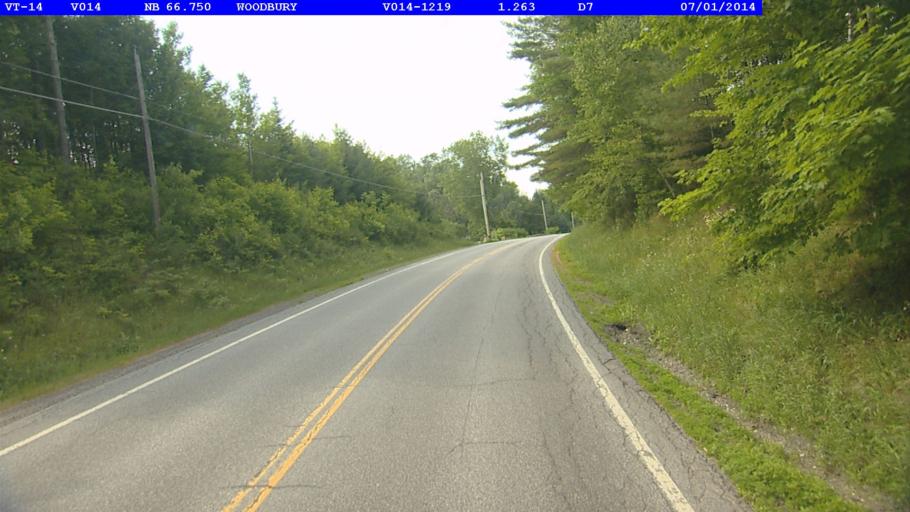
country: US
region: Vermont
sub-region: Caledonia County
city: Hardwick
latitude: 44.4095
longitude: -72.4190
